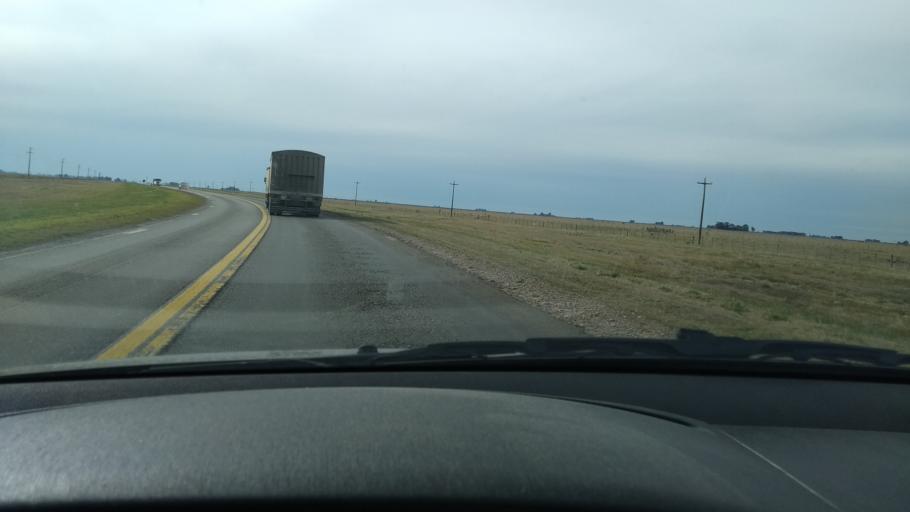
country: AR
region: Buenos Aires
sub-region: Partido de Azul
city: Azul
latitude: -36.7168
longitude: -59.7633
